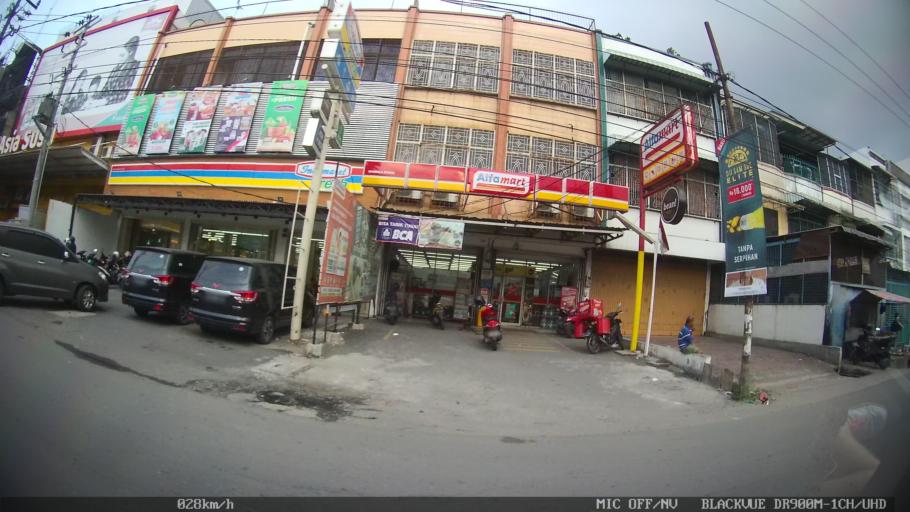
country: ID
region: North Sumatra
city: Medan
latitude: 3.5943
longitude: 98.7117
